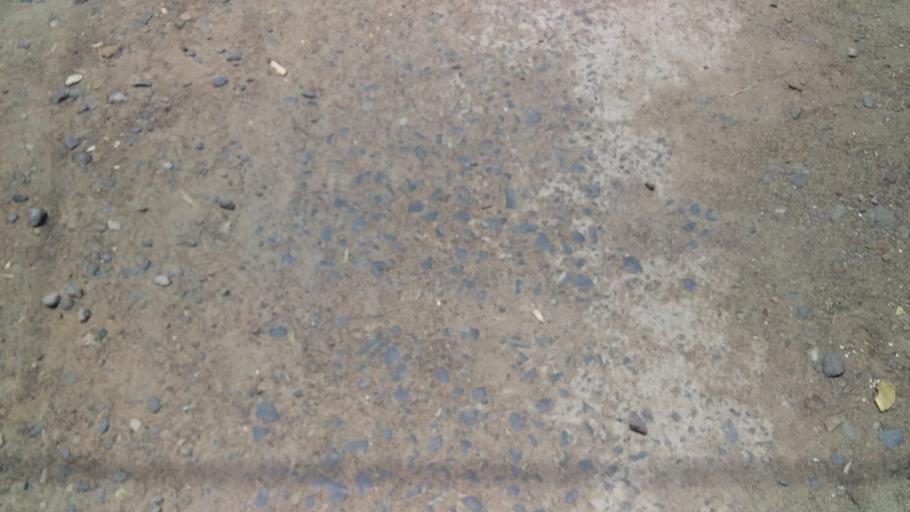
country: IN
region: Tamil Nadu
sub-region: Kancheepuram
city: Pallavaram
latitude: 12.9754
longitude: 80.1314
